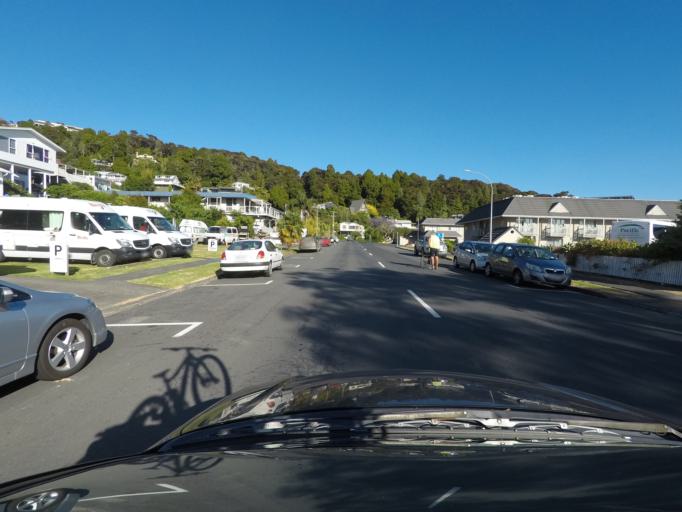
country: NZ
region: Northland
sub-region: Far North District
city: Paihia
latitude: -35.2814
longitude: 174.0901
